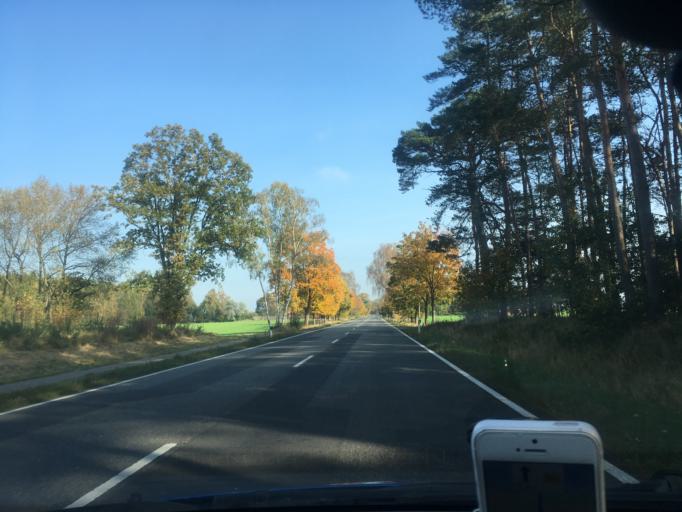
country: DE
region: Mecklenburg-Vorpommern
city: Stralendorf
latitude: 53.5525
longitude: 11.3293
